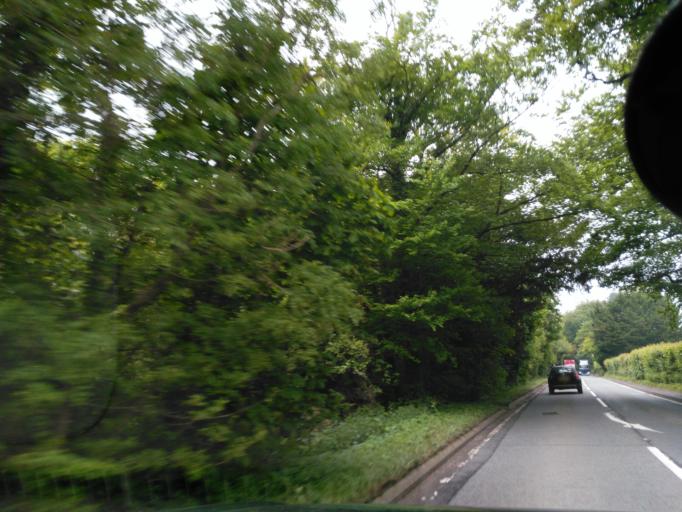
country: GB
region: England
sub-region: Somerset
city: Shepton Mallet
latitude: 51.1838
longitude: -2.5242
